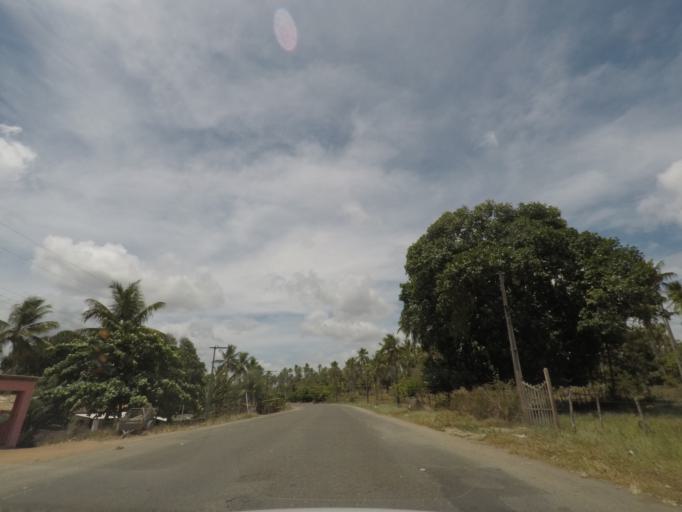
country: BR
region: Sergipe
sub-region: Indiaroba
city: Indiaroba
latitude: -11.5263
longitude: -37.5344
